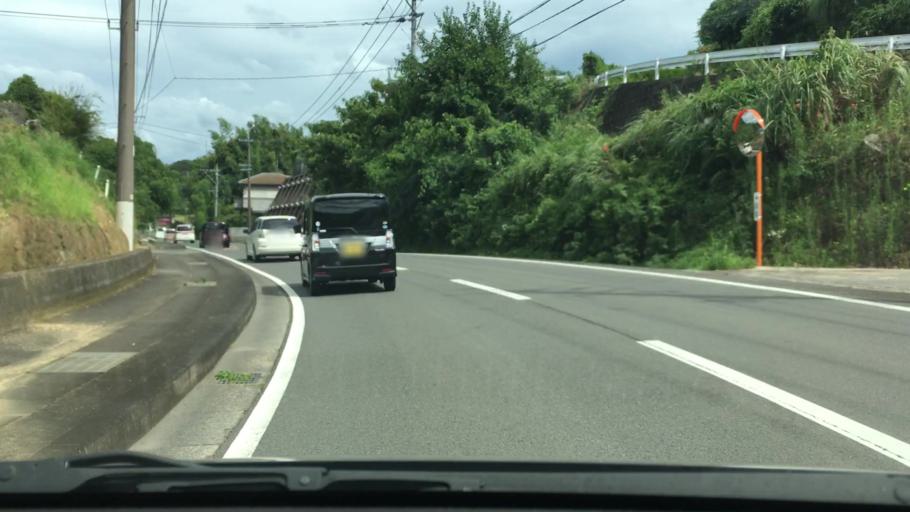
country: JP
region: Nagasaki
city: Togitsu
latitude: 32.9173
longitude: 129.7852
